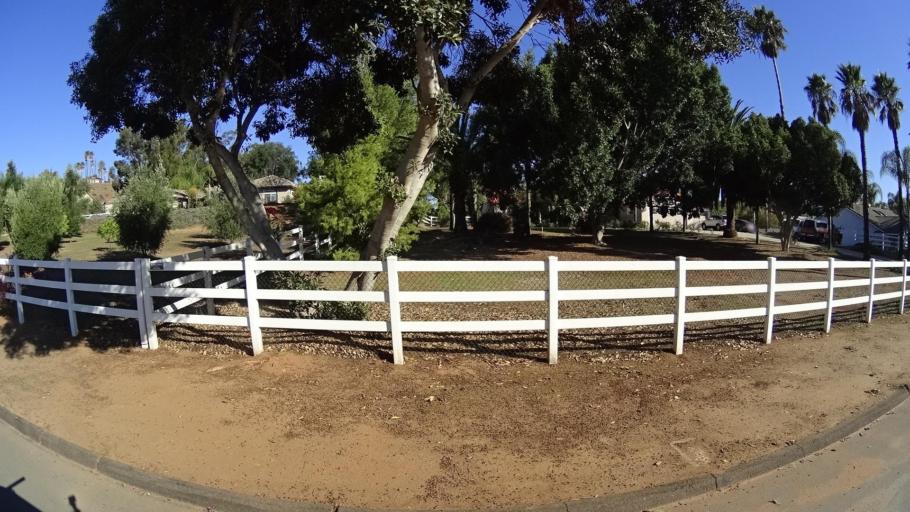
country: US
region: California
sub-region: San Diego County
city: Jamul
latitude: 32.7096
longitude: -116.8754
